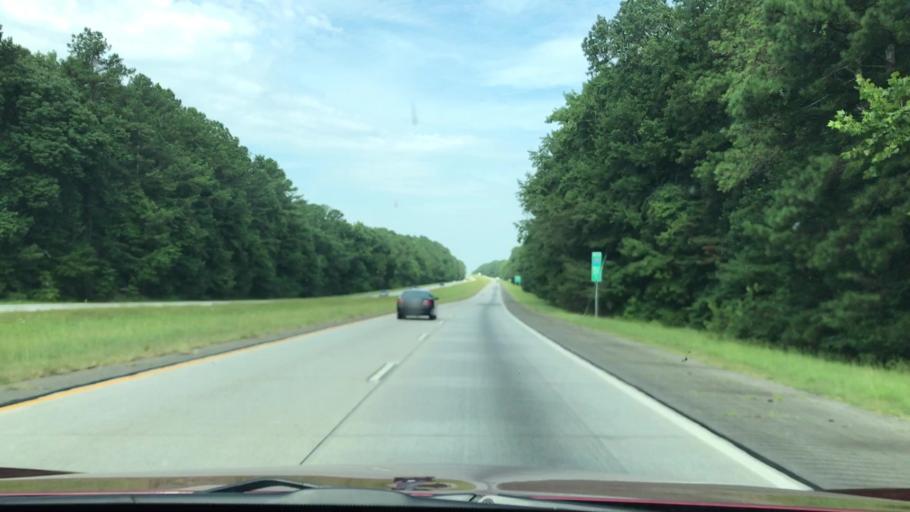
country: US
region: Georgia
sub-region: Warren County
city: Firing Range
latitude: 33.5008
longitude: -82.7833
